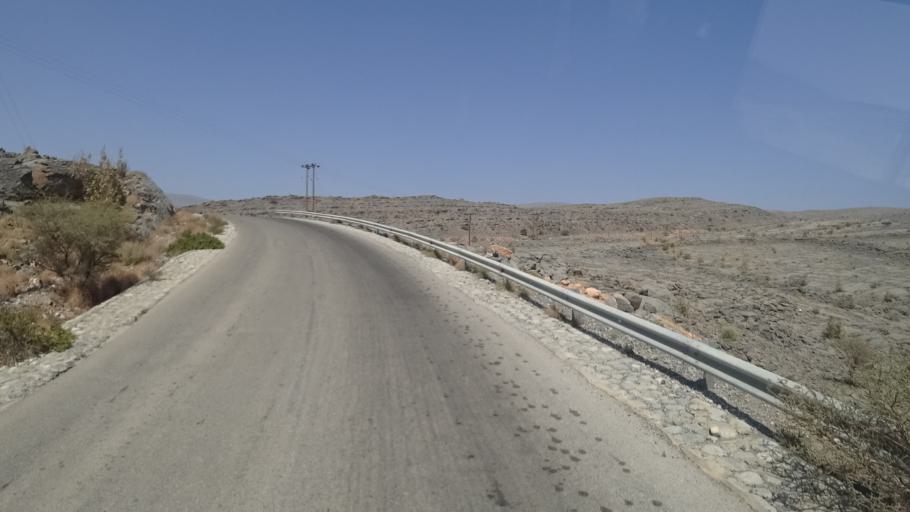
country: OM
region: Muhafazat ad Dakhiliyah
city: Bahla'
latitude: 23.0967
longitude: 57.3916
